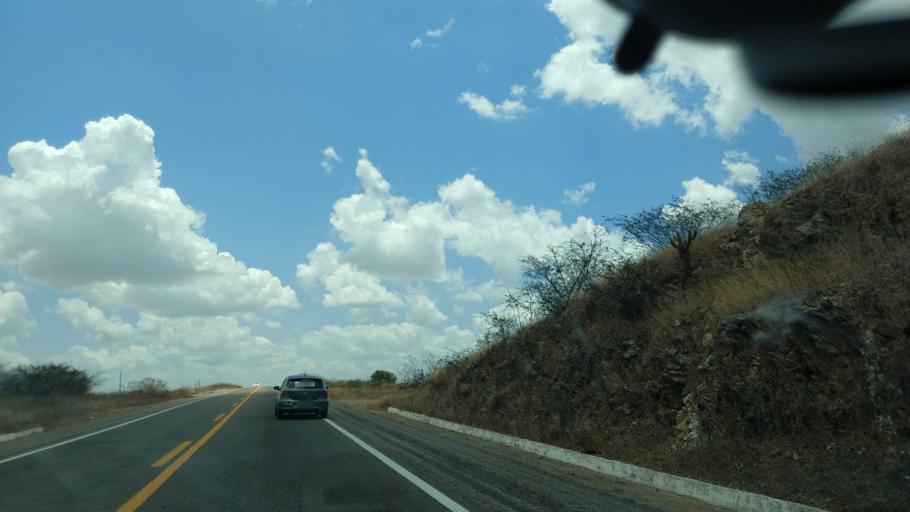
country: BR
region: Rio Grande do Norte
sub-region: Cerro Cora
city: Cerro Cora
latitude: -6.2004
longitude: -36.3379
